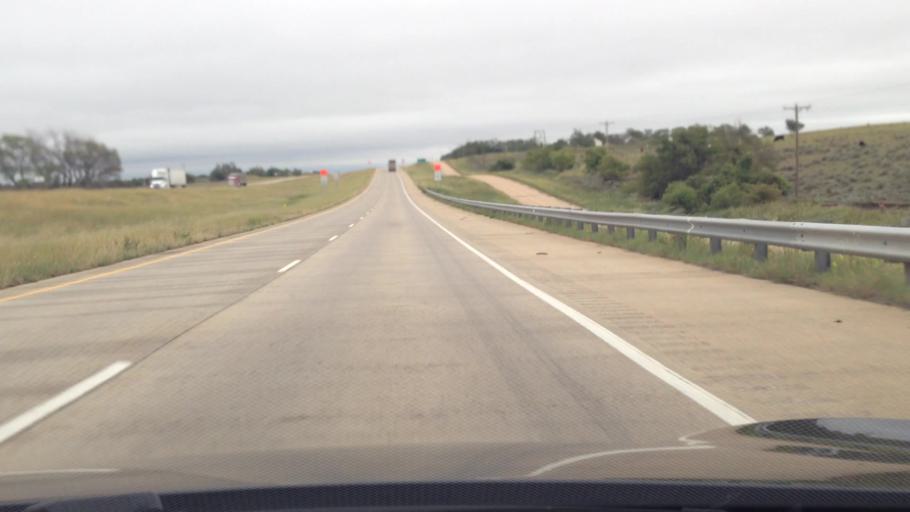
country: US
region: Texas
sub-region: Wheeler County
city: Shamrock
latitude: 35.2271
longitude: -100.4231
